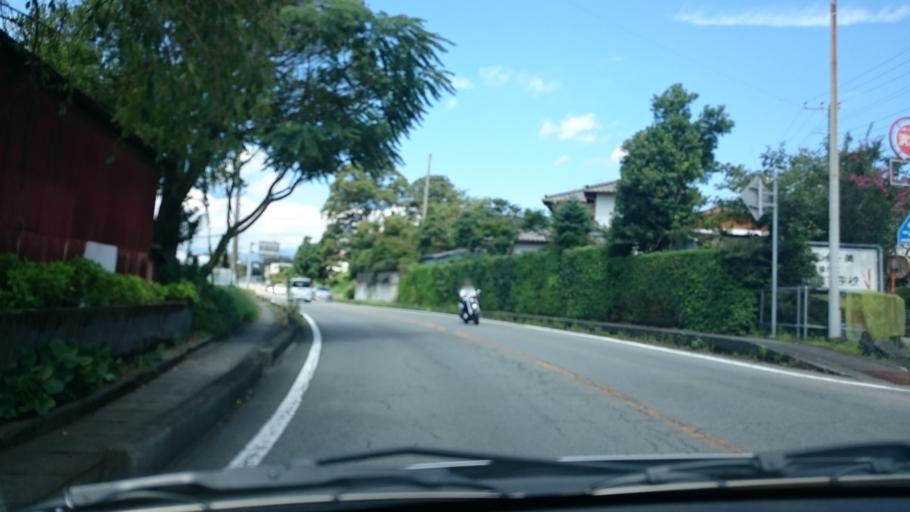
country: JP
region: Shizuoka
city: Gotemba
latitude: 35.2463
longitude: 138.9232
